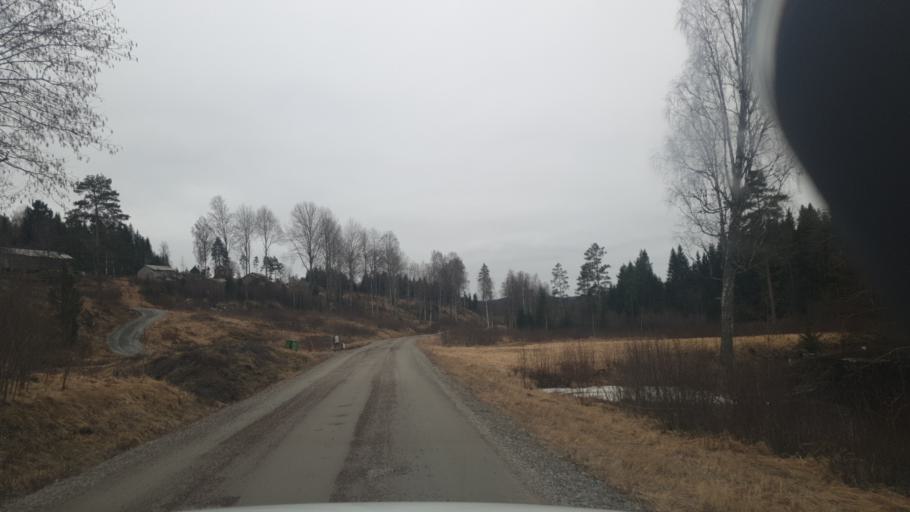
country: NO
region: Ostfold
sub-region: Romskog
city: Romskog
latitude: 59.6786
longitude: 11.9334
